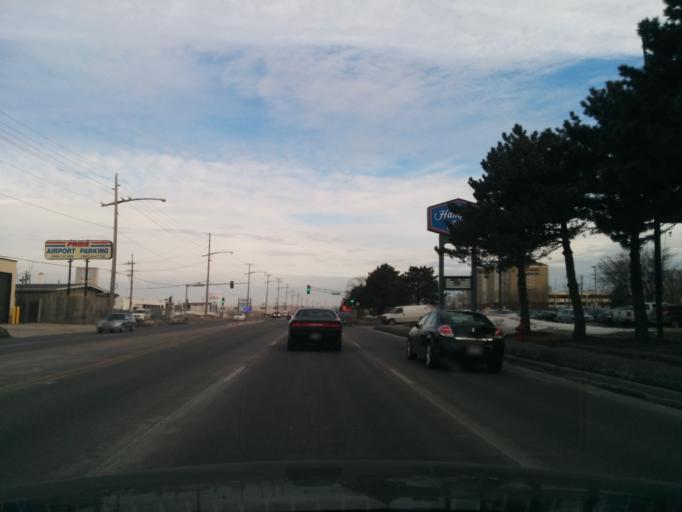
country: US
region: Illinois
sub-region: Cook County
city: Schiller Park
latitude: 41.9497
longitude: -87.8857
